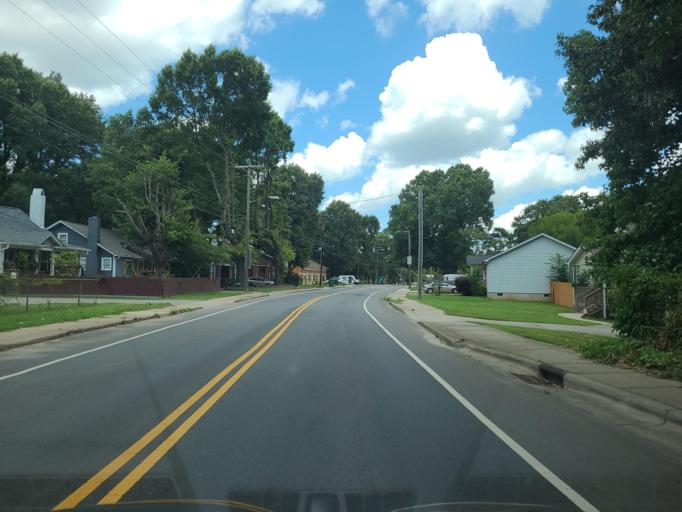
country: US
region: North Carolina
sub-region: Mecklenburg County
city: Charlotte
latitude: 35.2531
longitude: -80.8977
